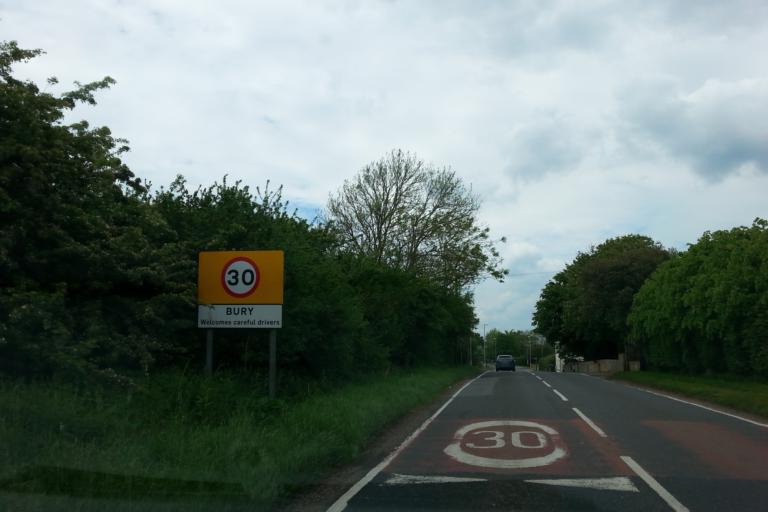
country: GB
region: England
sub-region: Cambridgeshire
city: Ramsey
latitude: 52.4344
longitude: -0.1061
